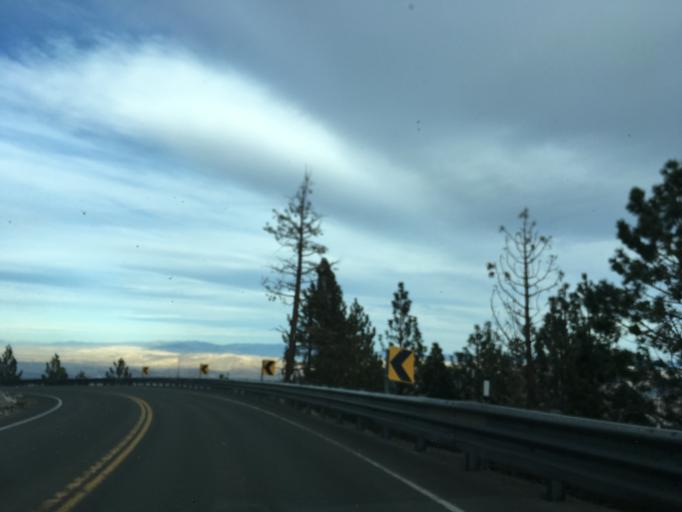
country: US
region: Nevada
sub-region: Washoe County
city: Incline Village
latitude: 39.3322
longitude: -119.8683
